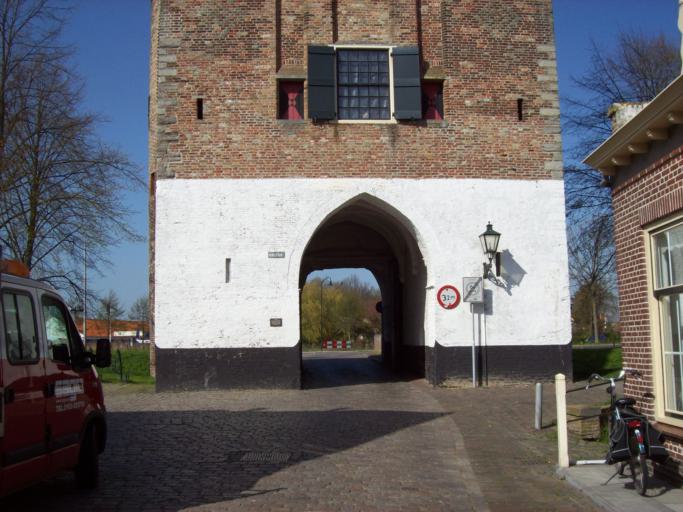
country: NL
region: Zeeland
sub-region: Schouwen-Duiveland
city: Scharendijke
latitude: 51.6534
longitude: 3.9195
